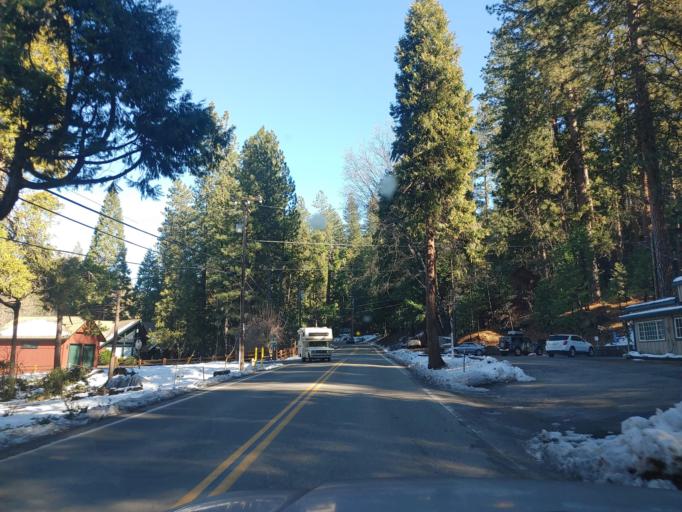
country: US
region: California
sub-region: Tuolumne County
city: Twain Harte
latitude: 38.0303
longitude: -120.2367
